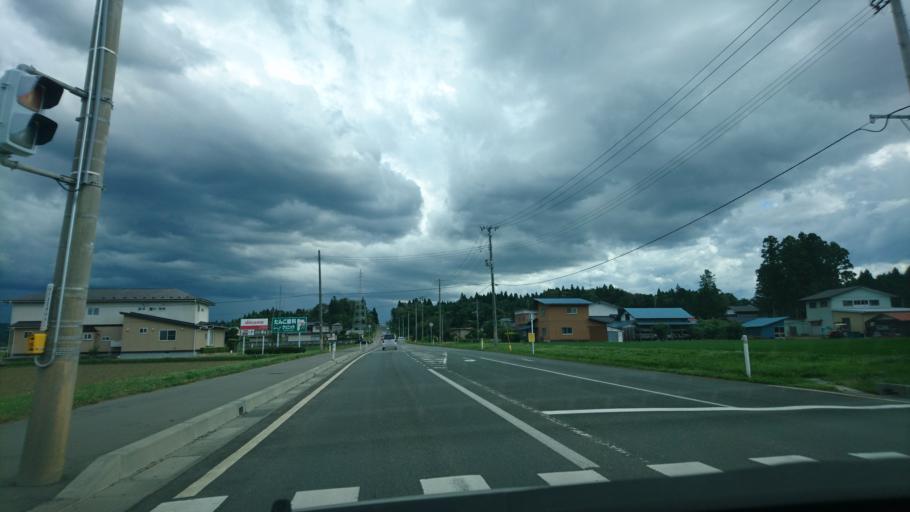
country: JP
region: Iwate
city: Kitakami
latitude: 39.3131
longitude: 141.1270
